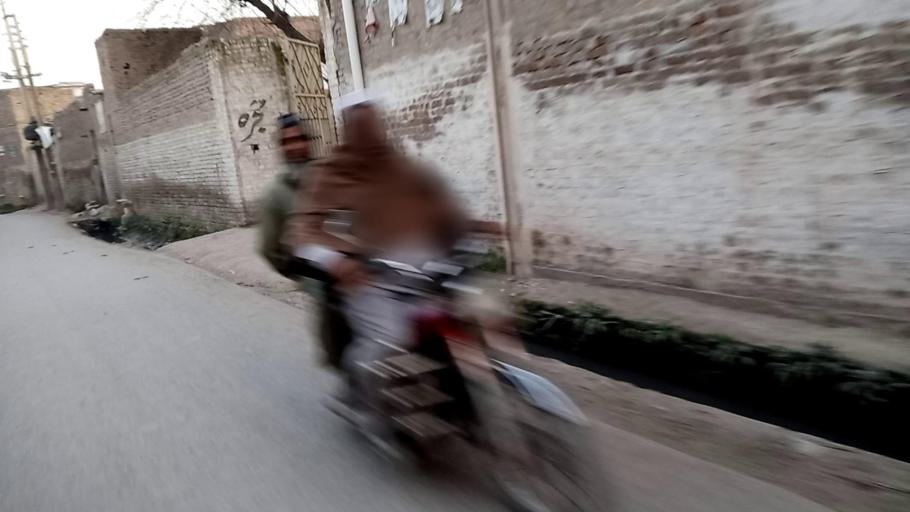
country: PK
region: Khyber Pakhtunkhwa
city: Peshawar
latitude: 34.0318
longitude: 71.4921
